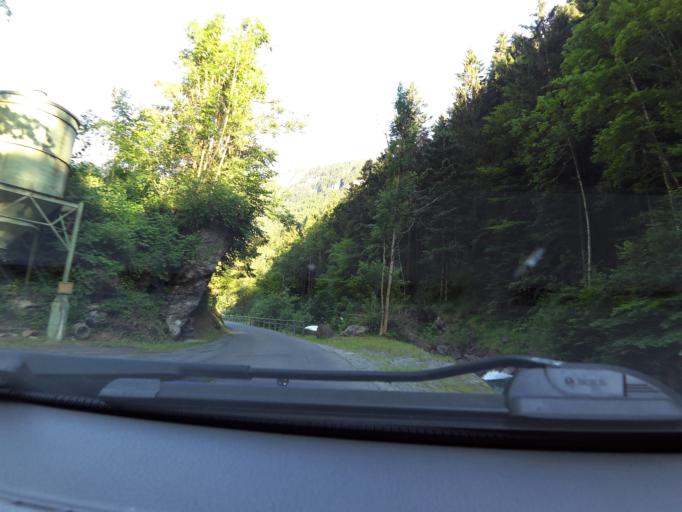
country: CH
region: Uri
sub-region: Uri
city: Bauen
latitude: 46.9121
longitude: 8.5531
